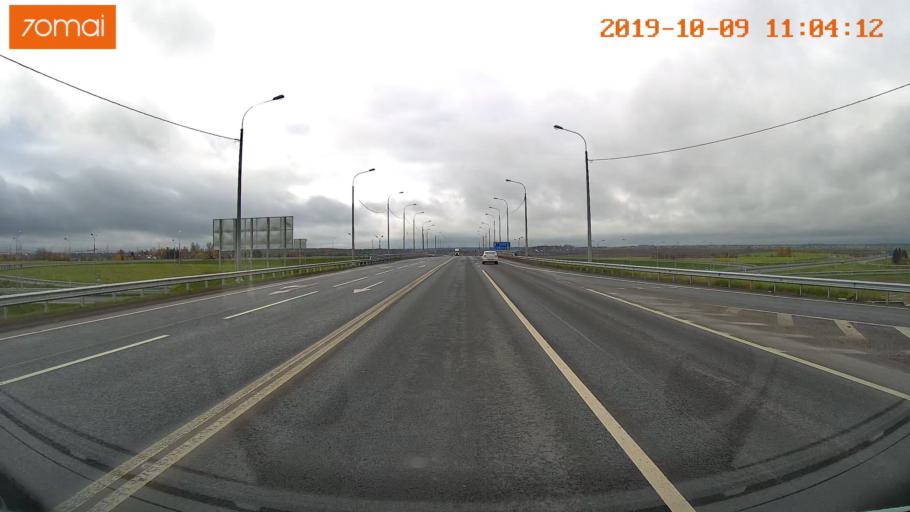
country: RU
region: Vologda
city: Vologda
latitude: 59.2144
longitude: 39.7699
